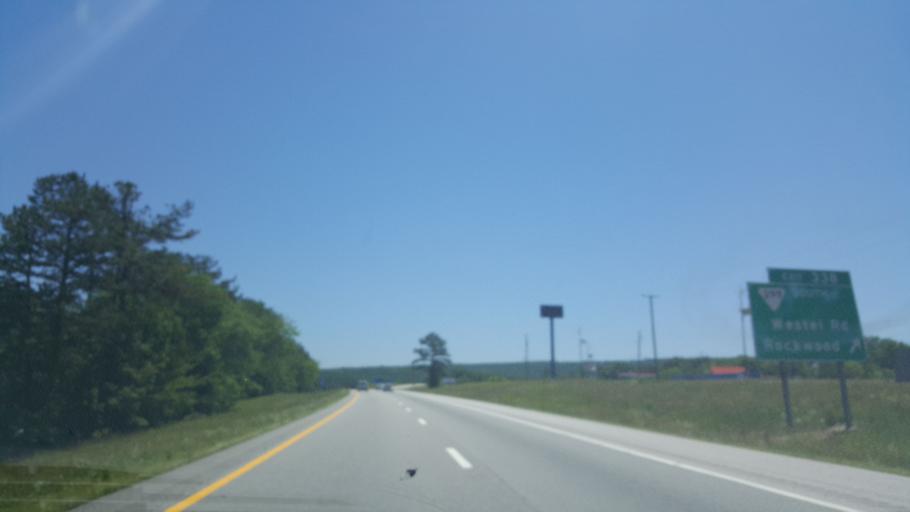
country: US
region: Tennessee
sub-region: Roane County
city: Rockwood
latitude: 35.8920
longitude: -84.7396
